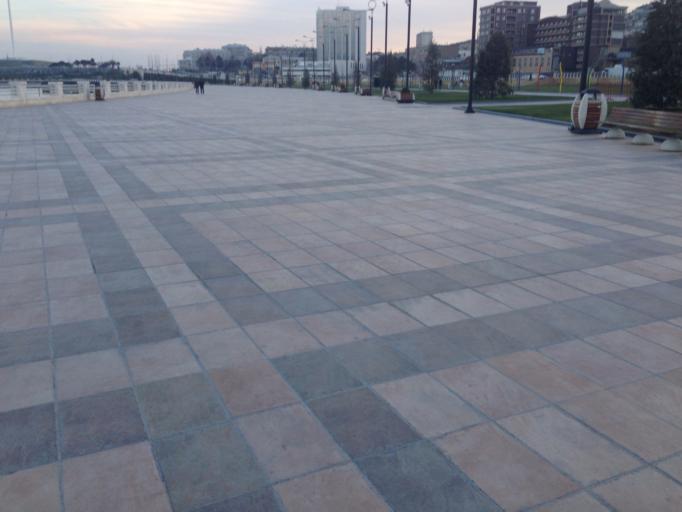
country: AZ
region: Baki
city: Badamdar
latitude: 40.3508
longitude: 49.8370
